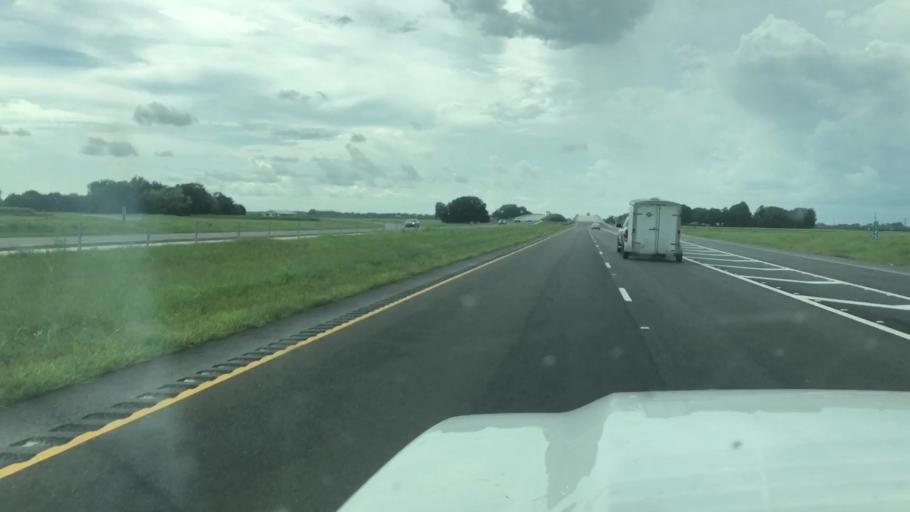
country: US
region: Louisiana
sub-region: Iberia Parish
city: Jeanerette
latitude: 29.8636
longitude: -91.6274
